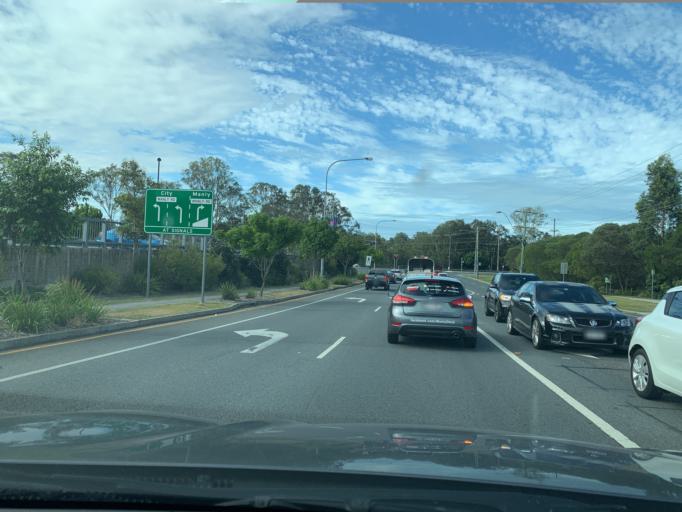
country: AU
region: Queensland
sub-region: Brisbane
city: Wynnum West
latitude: -27.4773
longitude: 153.1405
